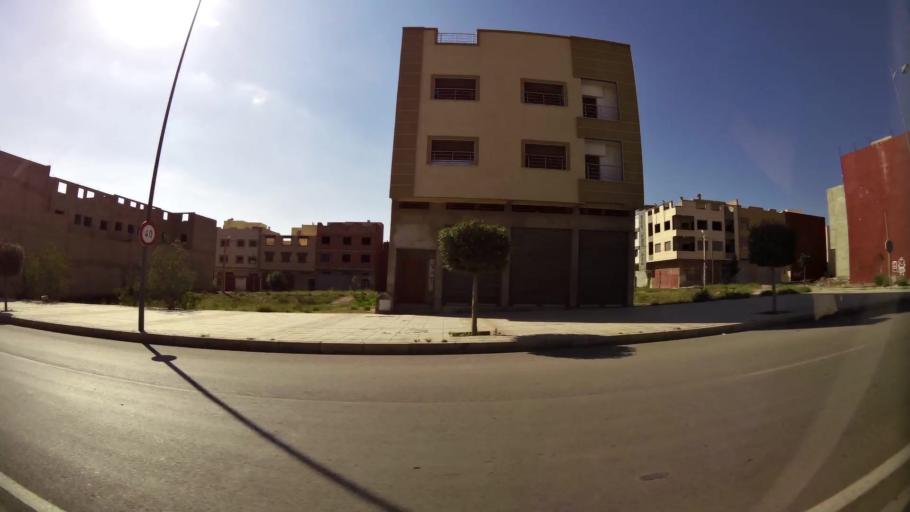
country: MA
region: Oriental
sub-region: Oujda-Angad
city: Oujda
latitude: 34.6610
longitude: -1.9492
